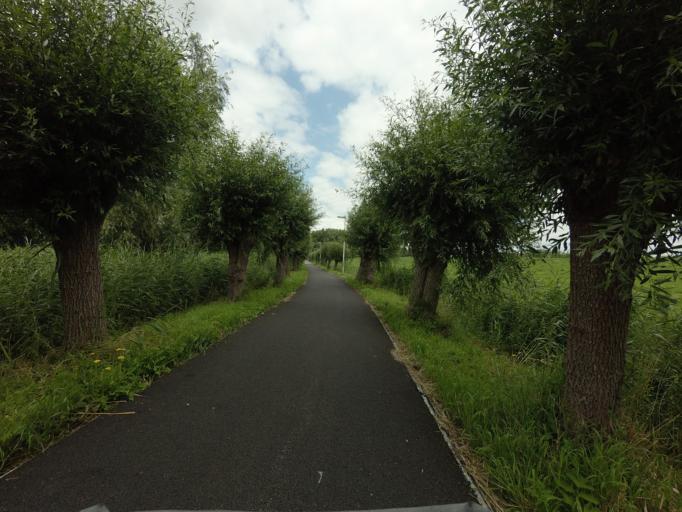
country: NL
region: South Holland
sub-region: Gemeente Waddinxveen
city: Vondelwijk
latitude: 52.0616
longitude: 4.6523
